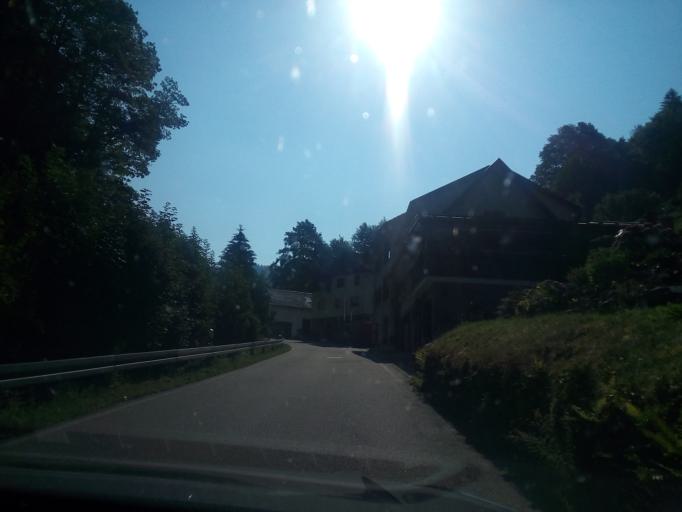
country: DE
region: Baden-Wuerttemberg
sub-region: Freiburg Region
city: Ottenhofen im Schwarzwald
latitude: 48.5456
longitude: 8.1696
